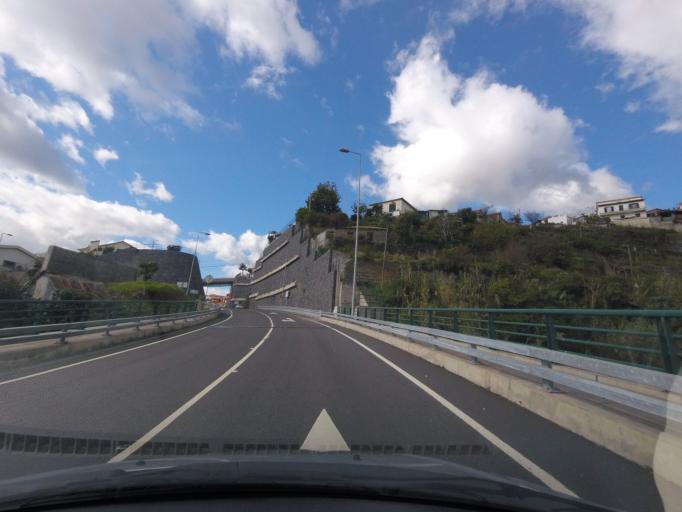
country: PT
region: Madeira
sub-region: Funchal
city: Nossa Senhora do Monte
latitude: 32.6787
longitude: -16.9416
